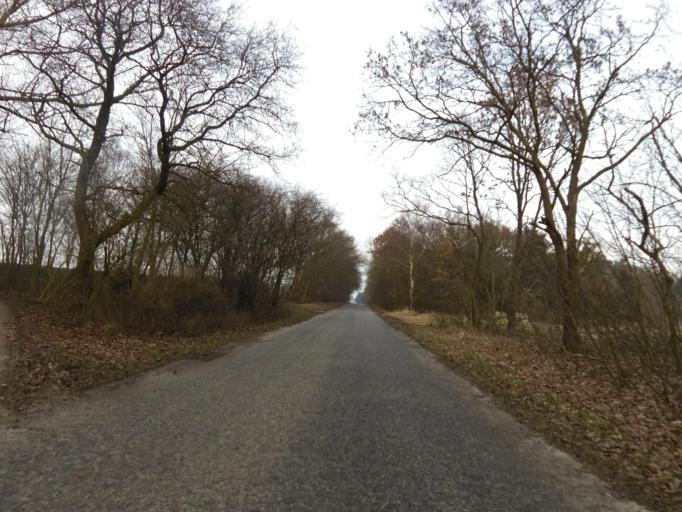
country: DK
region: South Denmark
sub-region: Esbjerg Kommune
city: Ribe
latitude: 55.3367
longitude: 8.8890
